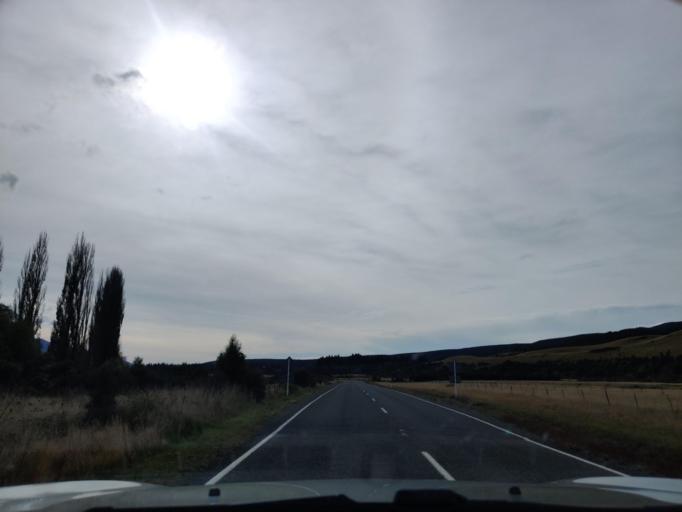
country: NZ
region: Tasman
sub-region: Tasman District
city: Brightwater
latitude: -41.6840
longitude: 173.1648
